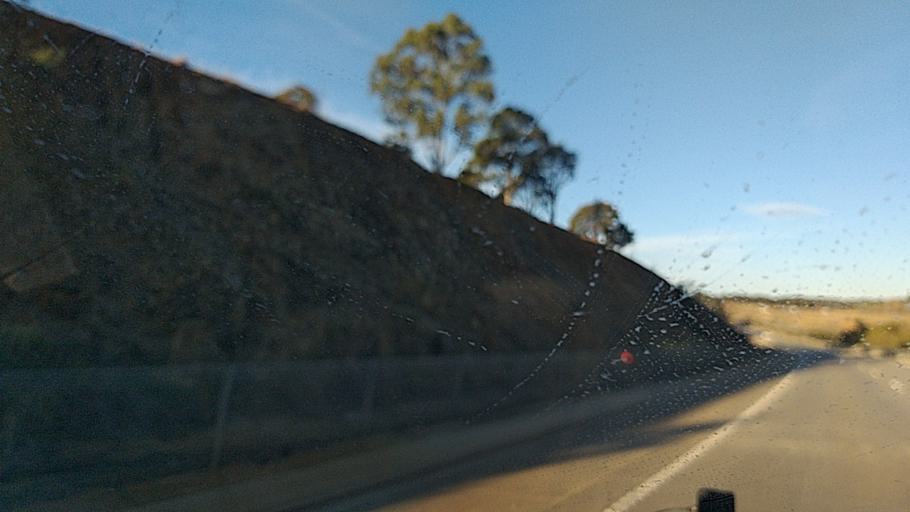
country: AU
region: New South Wales
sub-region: Yass Valley
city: Gundaroo
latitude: -35.1184
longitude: 149.3499
